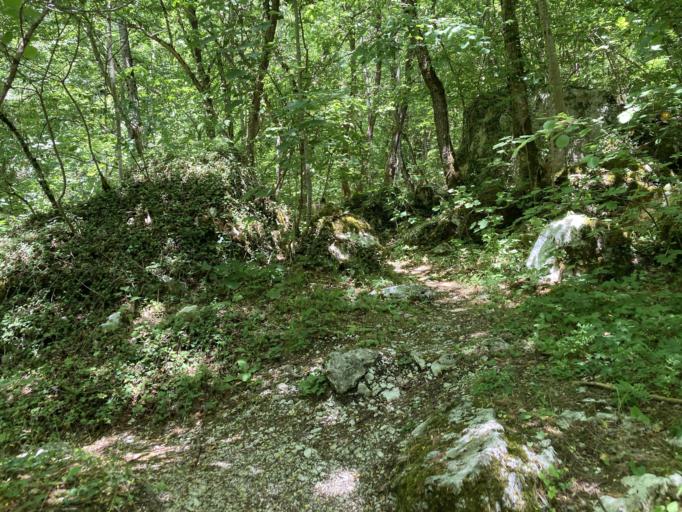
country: IT
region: Abruzzo
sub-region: Provincia dell' Aquila
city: Aielli
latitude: 42.1167
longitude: 13.5713
